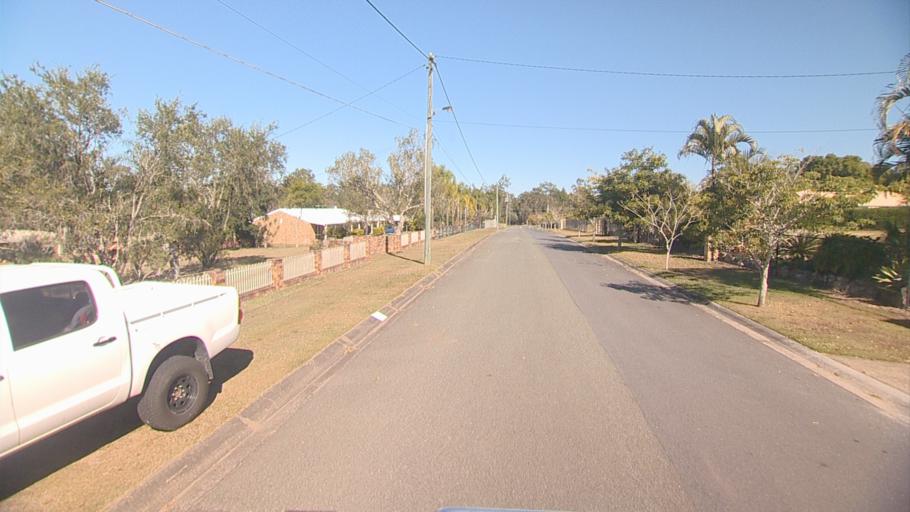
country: AU
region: Queensland
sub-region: Logan
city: Logan Reserve
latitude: -27.7037
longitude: 153.0707
